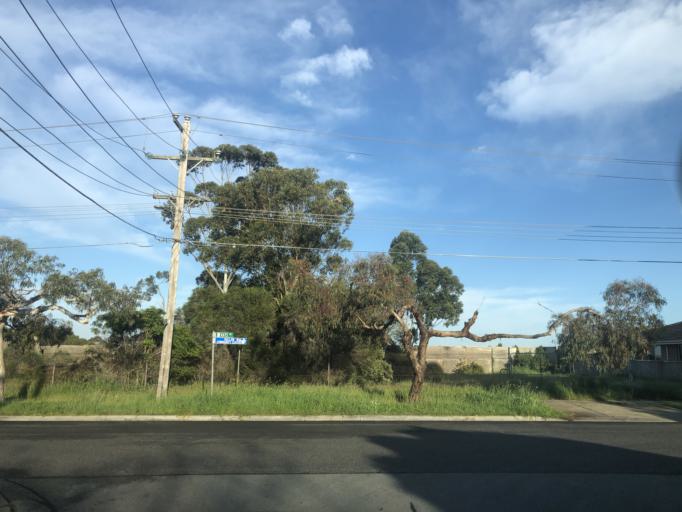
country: AU
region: Victoria
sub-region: Casey
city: Eumemmerring
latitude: -38.0026
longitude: 145.2535
